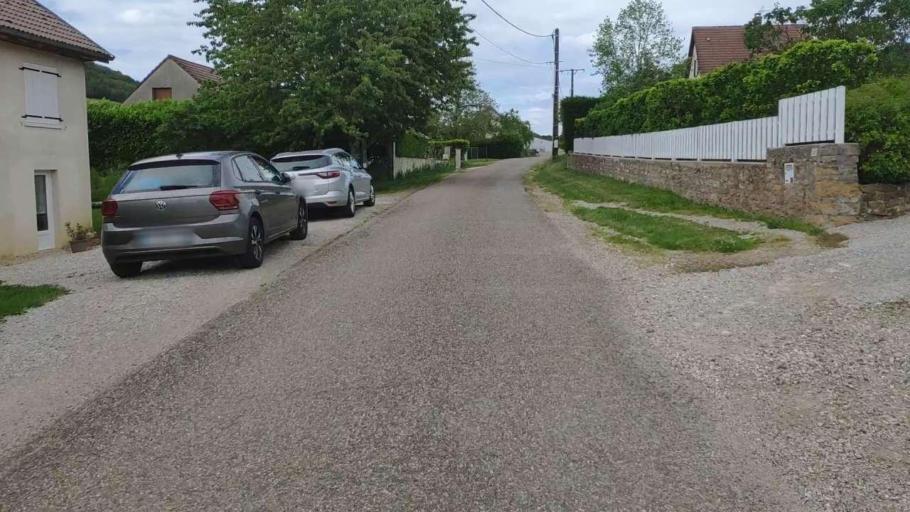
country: FR
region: Franche-Comte
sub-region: Departement du Jura
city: Perrigny
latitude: 46.7821
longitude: 5.5804
